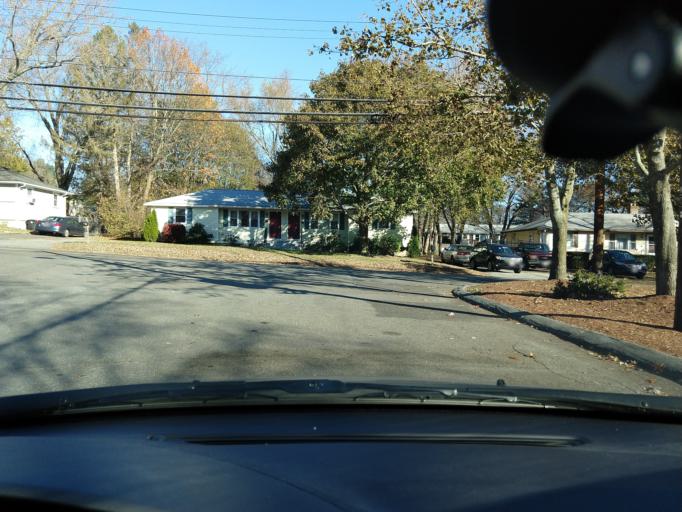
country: US
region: Massachusetts
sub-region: Middlesex County
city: Bedford
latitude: 42.4738
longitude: -71.2658
